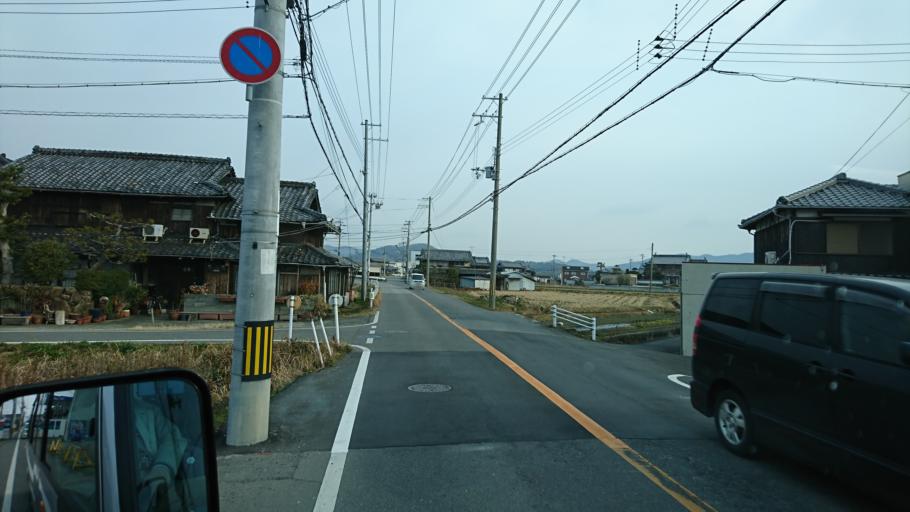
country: JP
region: Hyogo
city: Kakogawacho-honmachi
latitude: 34.8074
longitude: 134.8186
